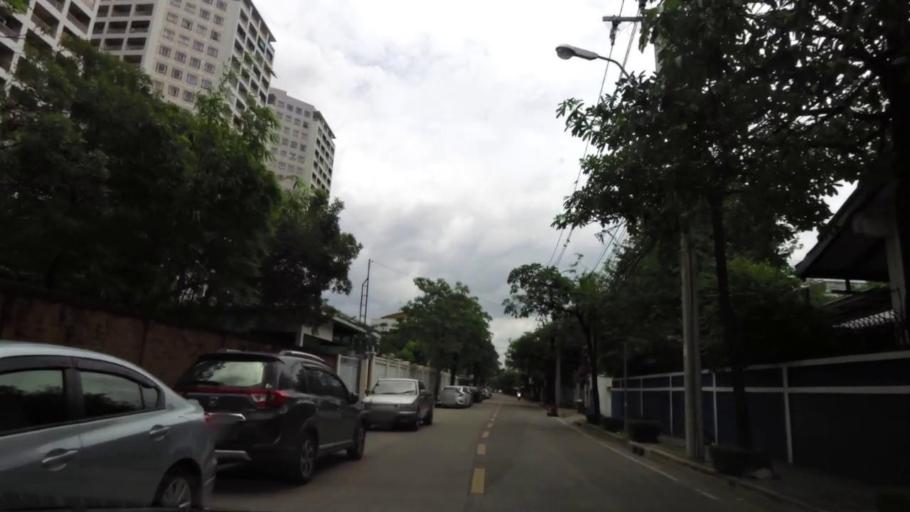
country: TH
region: Bangkok
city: Bang Kapi
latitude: 13.7561
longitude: 100.6395
